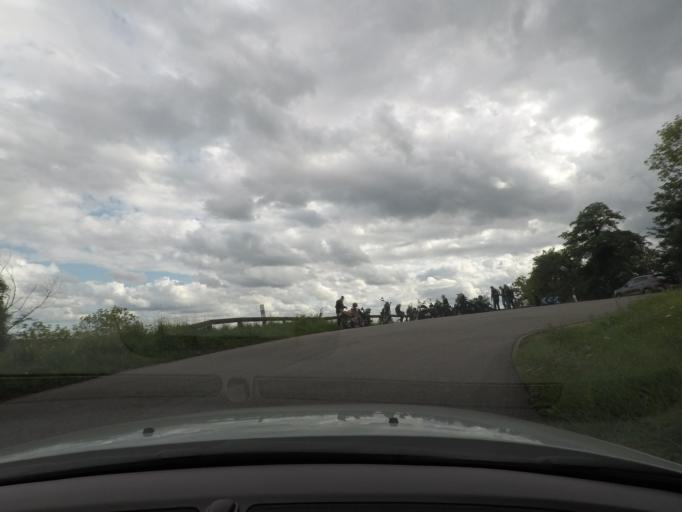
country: FR
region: Haute-Normandie
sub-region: Departement de l'Eure
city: Les Andelys
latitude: 49.2546
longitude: 1.3766
